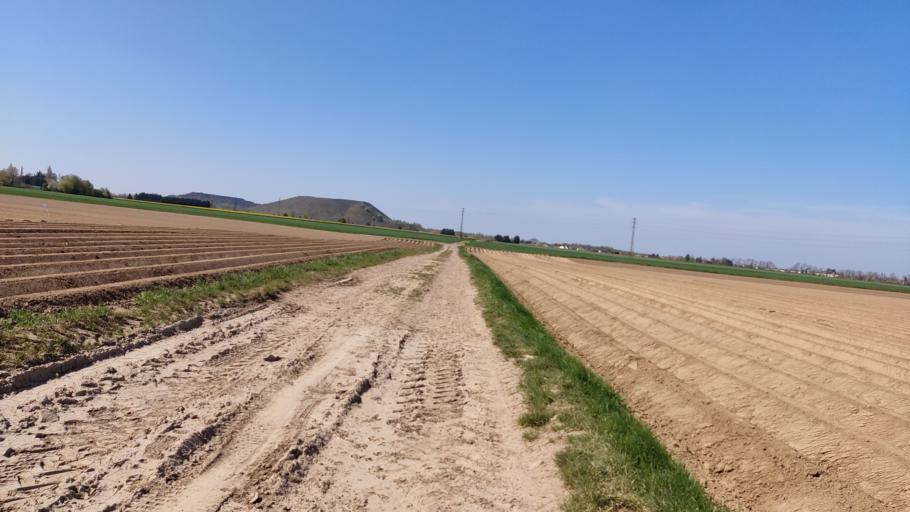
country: FR
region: Nord-Pas-de-Calais
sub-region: Departement du Pas-de-Calais
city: Henin-Beaumont
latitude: 50.3968
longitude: 2.9535
